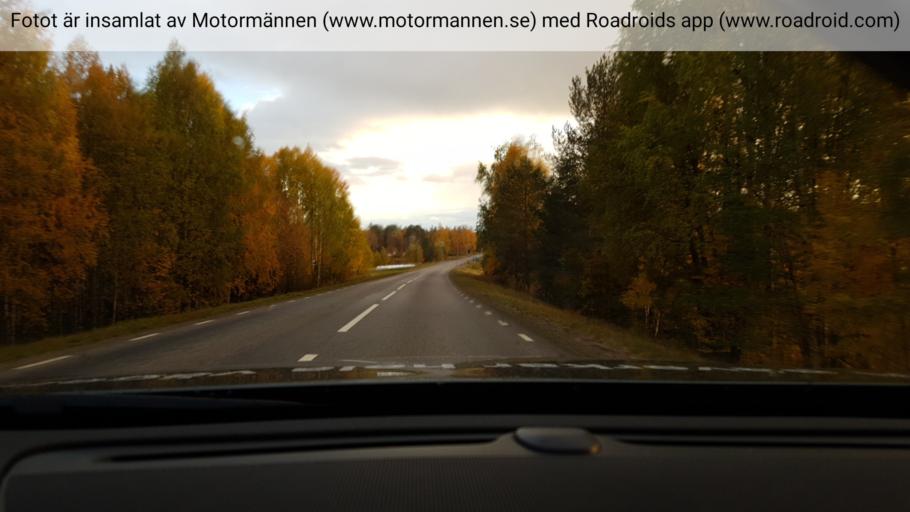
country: SE
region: Norrbotten
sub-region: Overkalix Kommun
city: OEverkalix
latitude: 66.5152
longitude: 22.7661
